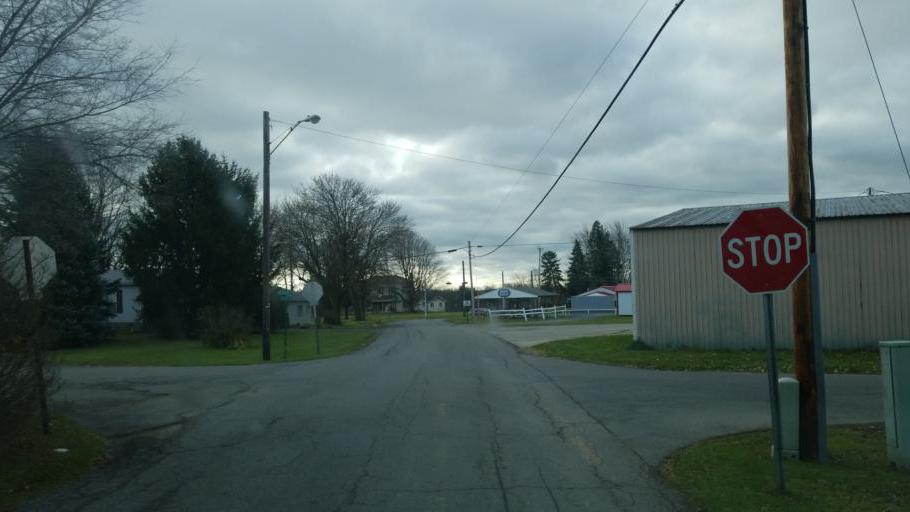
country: US
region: Ohio
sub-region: Hardin County
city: Kenton
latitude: 40.6515
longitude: -83.6212
